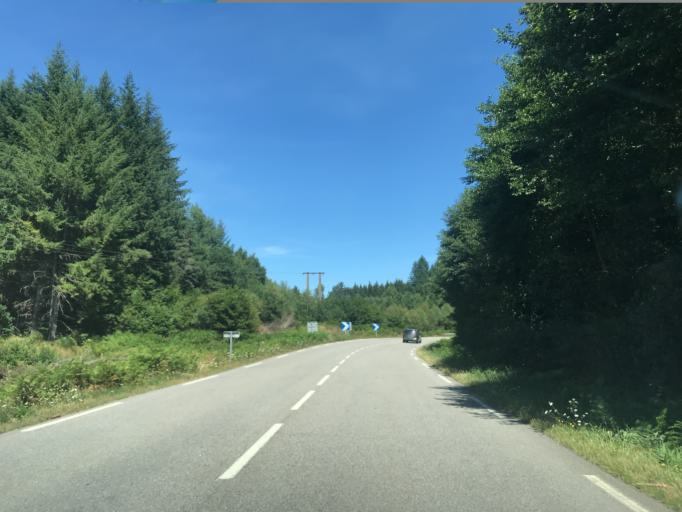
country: FR
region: Limousin
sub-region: Departement de la Correze
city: Egletons
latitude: 45.4532
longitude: 2.1125
